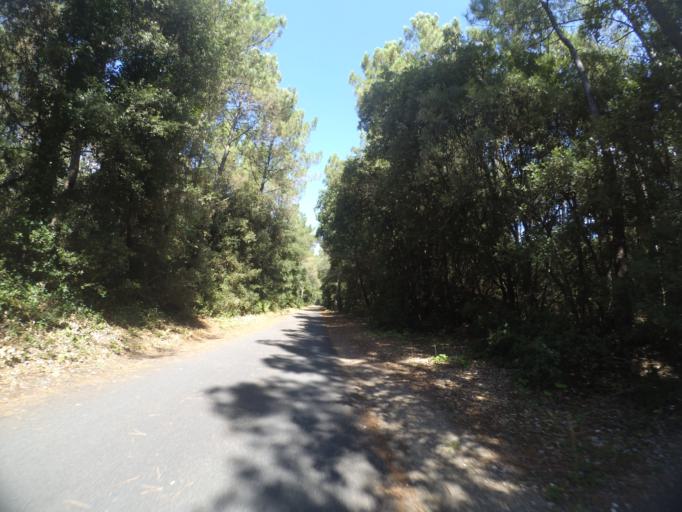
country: FR
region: Poitou-Charentes
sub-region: Departement de la Charente-Maritime
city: Les Mathes
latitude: 45.6752
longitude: -1.1512
